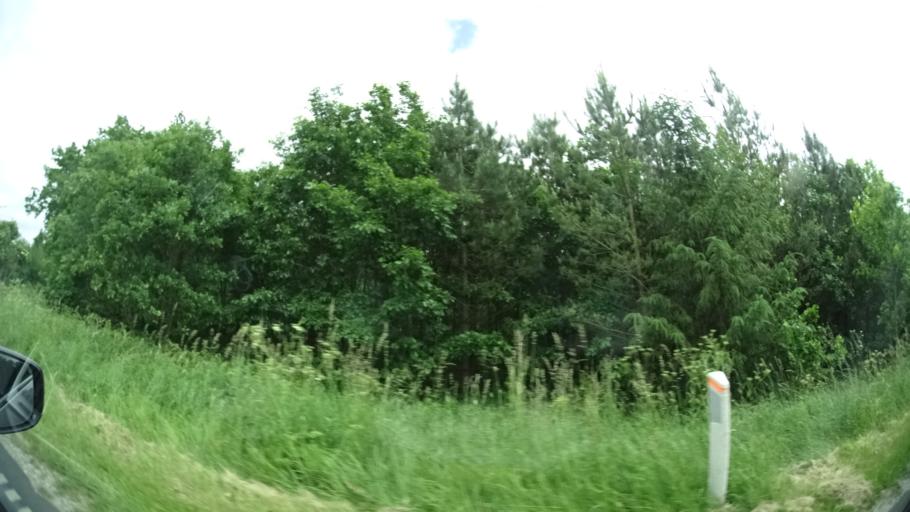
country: DK
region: Central Jutland
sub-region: Syddjurs Kommune
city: Ryomgard
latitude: 56.3618
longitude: 10.4949
